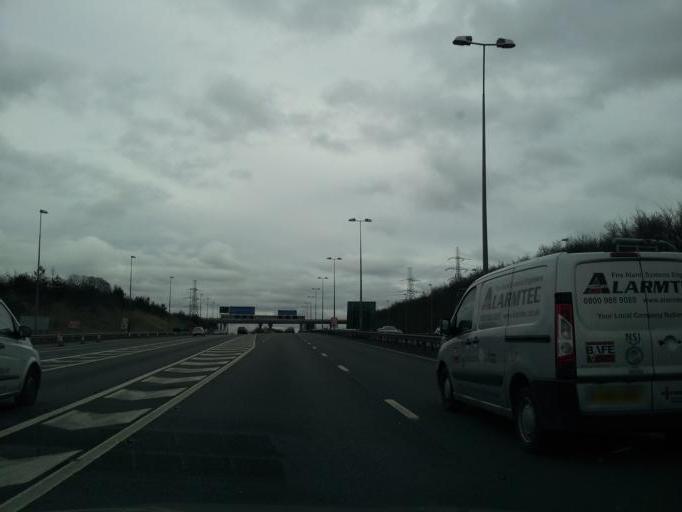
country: GB
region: England
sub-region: Staffordshire
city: Featherstone
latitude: 52.6725
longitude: -2.0791
